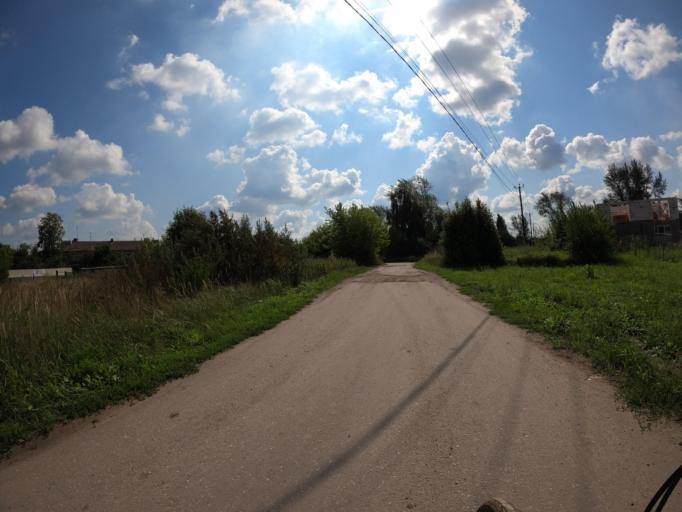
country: RU
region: Moskovskaya
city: Lopatinskiy
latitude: 55.3131
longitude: 38.7073
